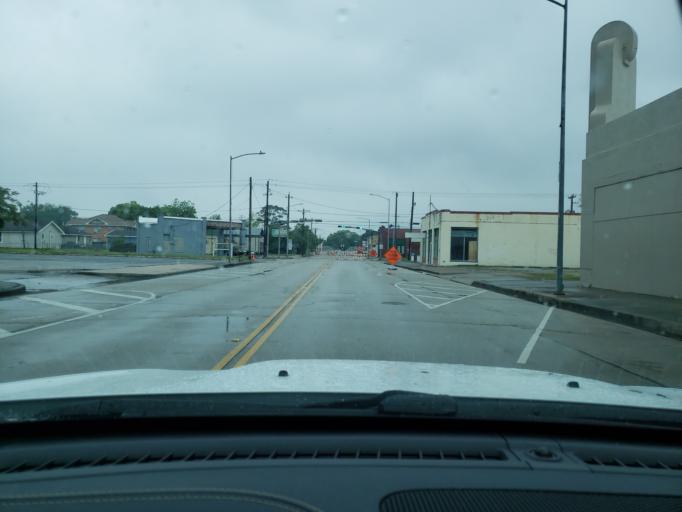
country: US
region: Texas
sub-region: Harris County
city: Baytown
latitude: 29.7335
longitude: -94.9719
